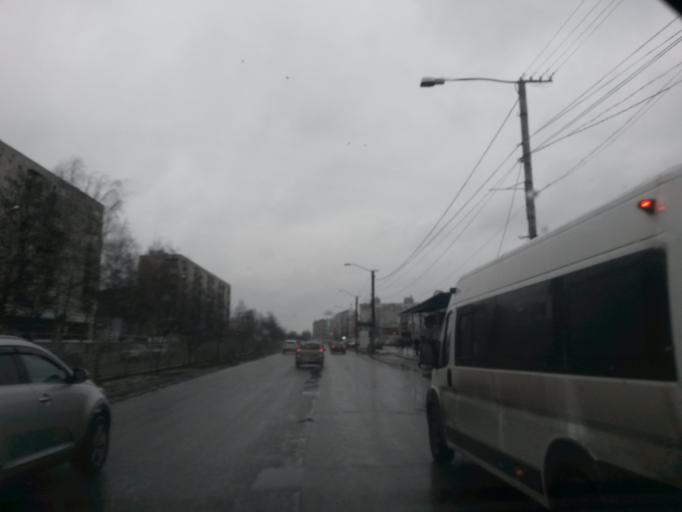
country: RU
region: Jaroslavl
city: Yaroslavl
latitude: 57.6481
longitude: 39.9519
